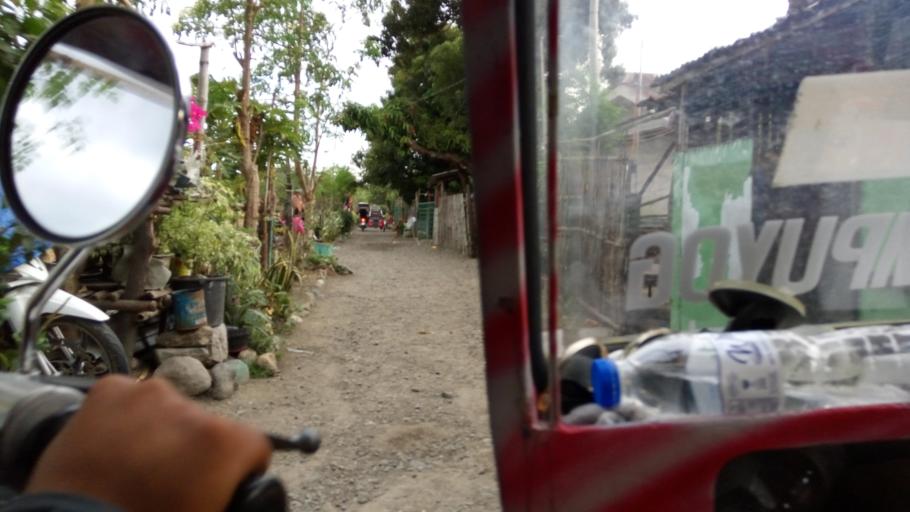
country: PH
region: Ilocos
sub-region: Province of La Union
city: Damortis
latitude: 16.2538
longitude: 120.4005
